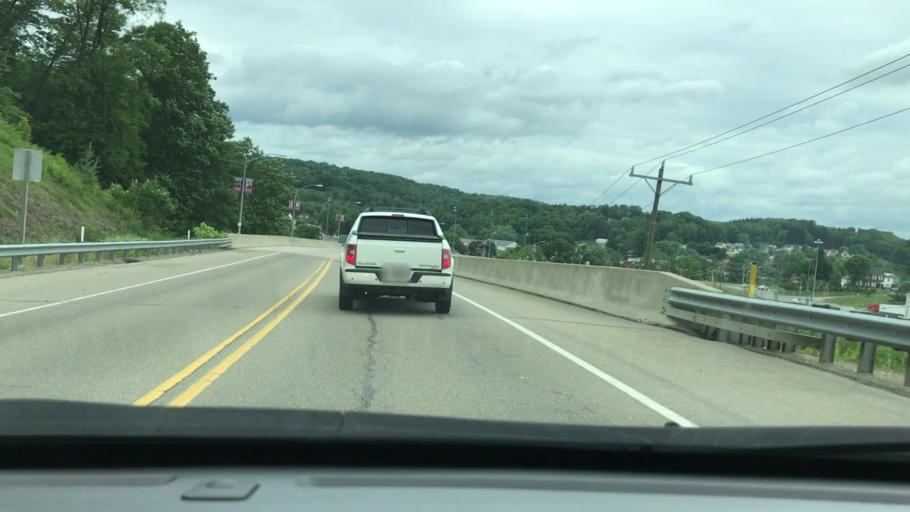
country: US
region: Pennsylvania
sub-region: Elk County
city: Johnsonburg
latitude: 41.4929
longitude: -78.6819
